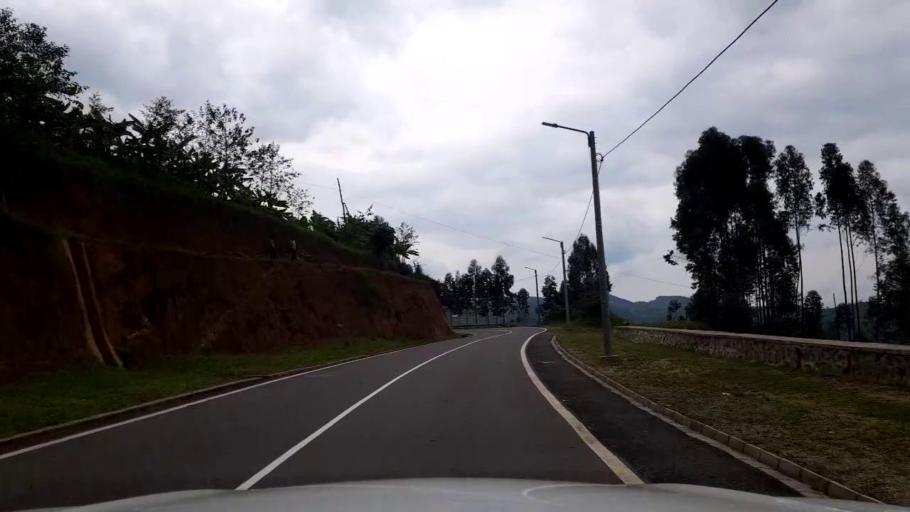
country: RW
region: Western Province
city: Kibuye
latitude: -1.9304
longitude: 29.3725
